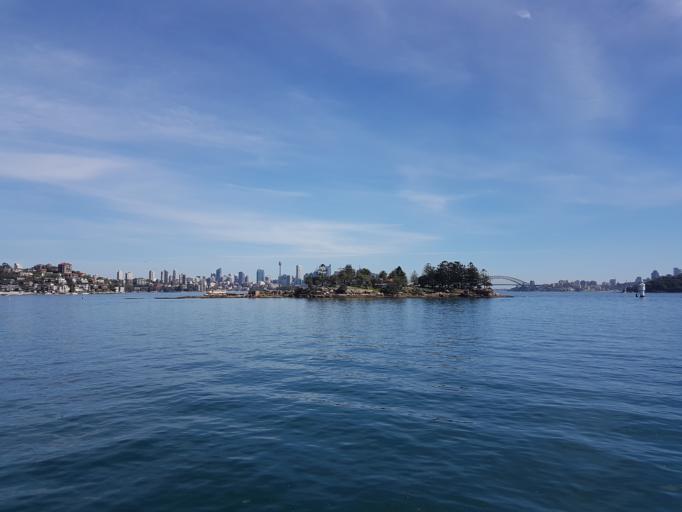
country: AU
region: New South Wales
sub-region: Woollahra
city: Point Piper
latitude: -33.8582
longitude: 151.2624
